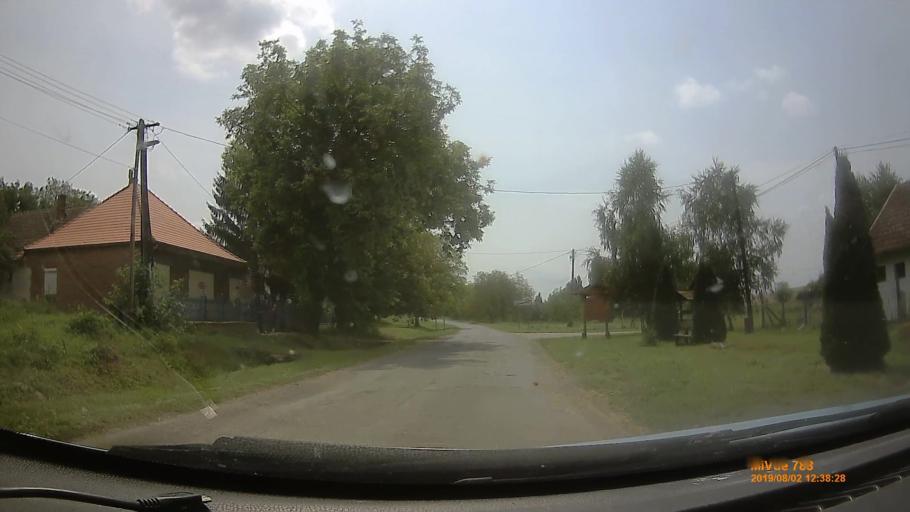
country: HU
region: Baranya
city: Buekkoesd
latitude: 46.0955
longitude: 17.9571
